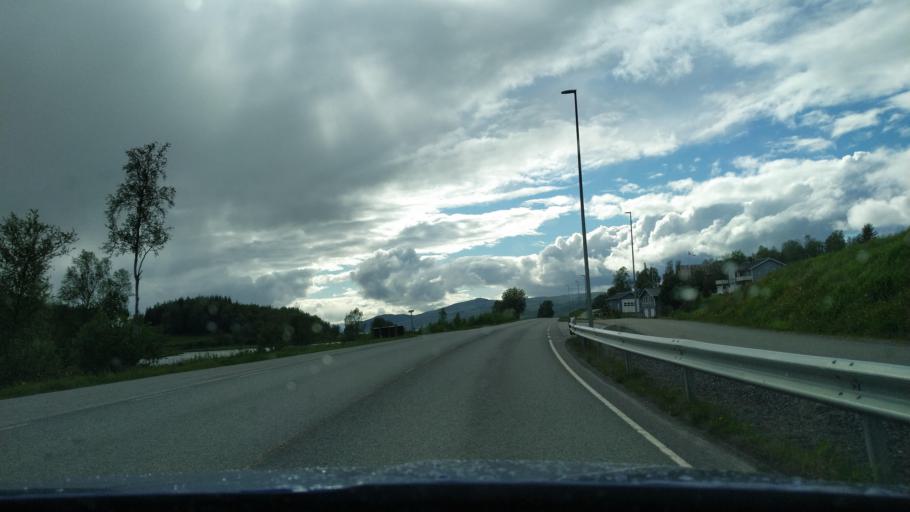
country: NO
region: Troms
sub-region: Sorreisa
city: Sorreisa
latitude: 69.1737
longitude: 18.0931
